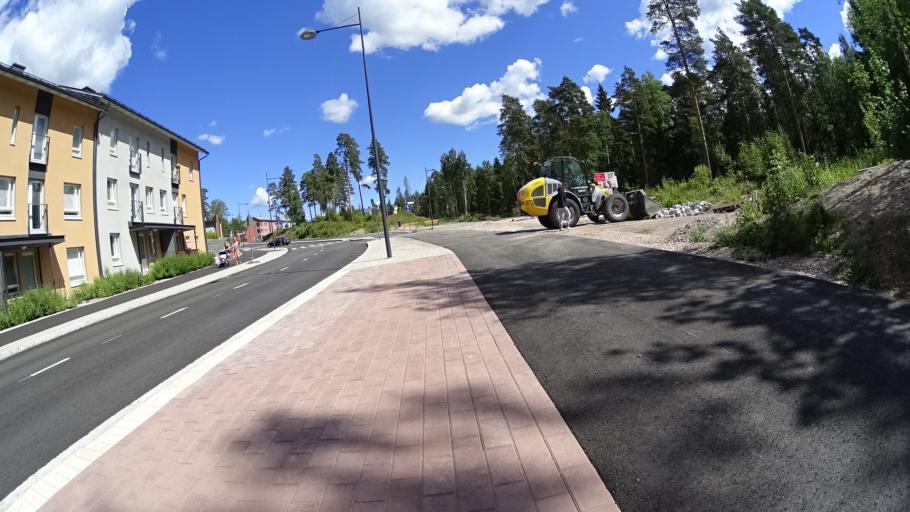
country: FI
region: Uusimaa
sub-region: Helsinki
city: Espoo
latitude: 60.1962
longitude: 24.6043
